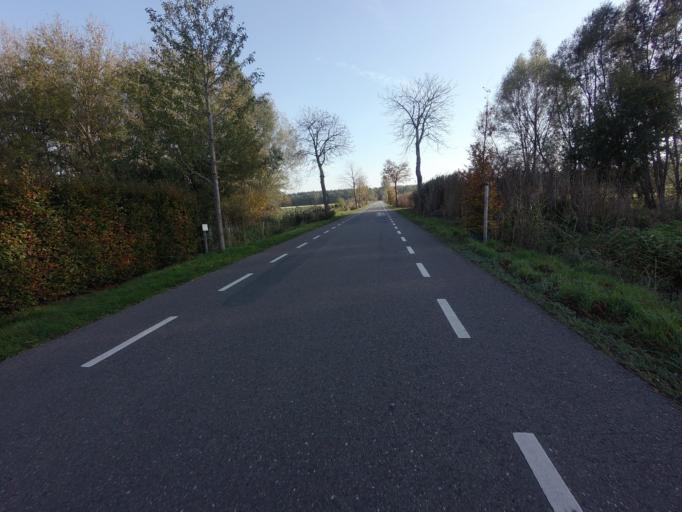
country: DE
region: North Rhine-Westphalia
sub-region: Regierungsbezirk Koln
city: Waldfeucht
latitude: 51.1005
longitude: 5.9894
